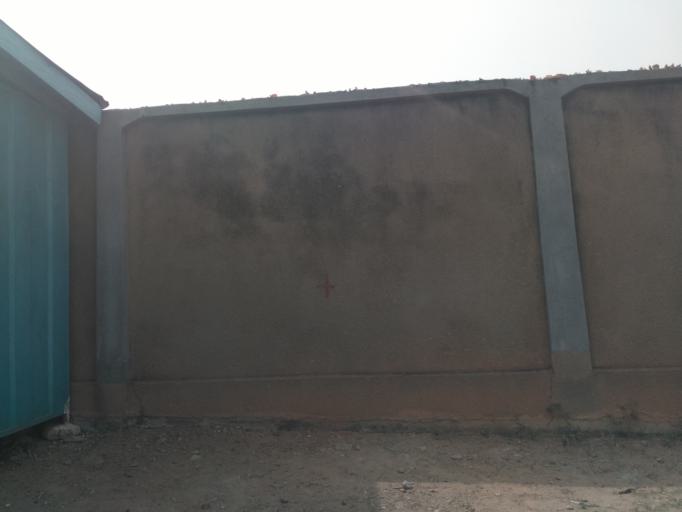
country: GH
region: Ashanti
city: Kumasi
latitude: 6.6802
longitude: -1.6006
